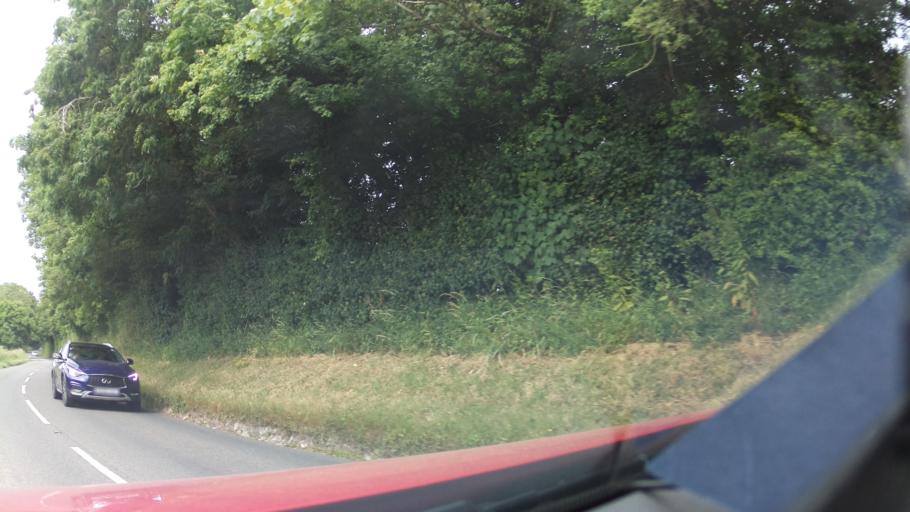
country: GB
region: England
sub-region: Devon
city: Colyton
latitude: 50.7239
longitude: -3.0478
